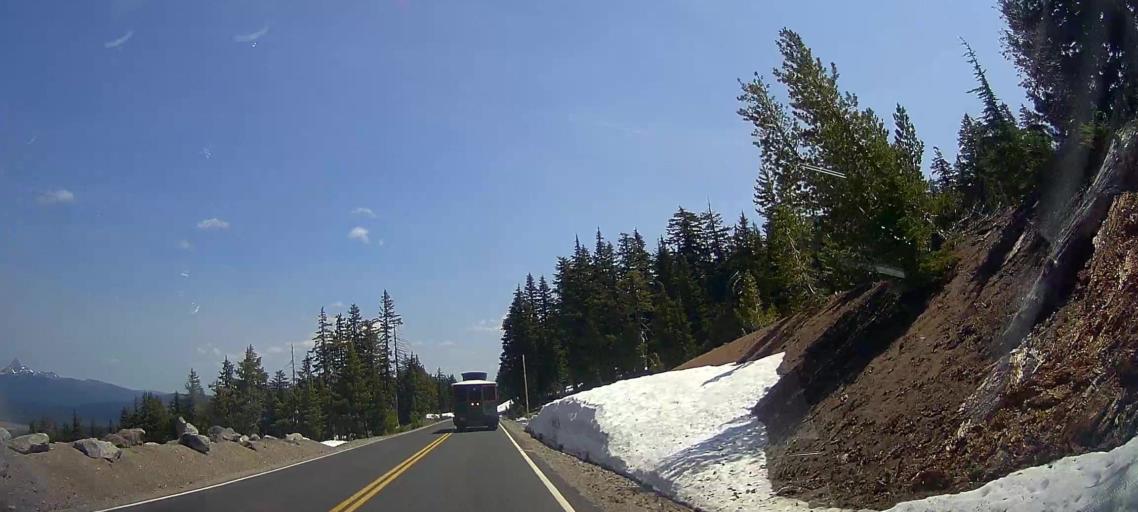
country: US
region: Oregon
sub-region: Jackson County
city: Shady Cove
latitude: 42.9801
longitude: -122.1399
